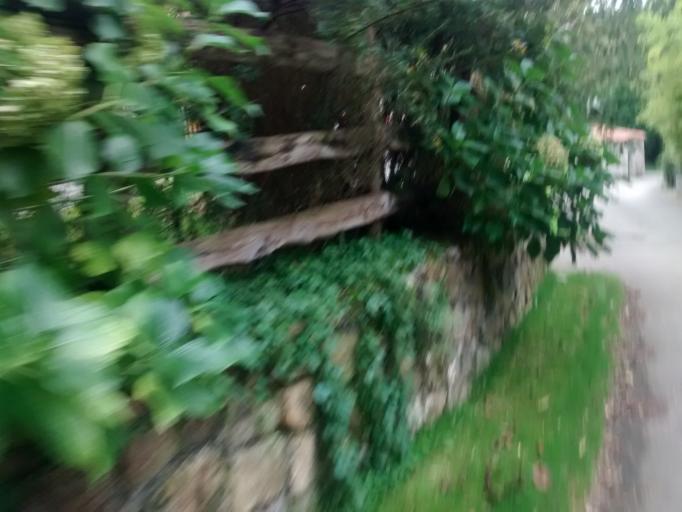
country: ES
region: Cantabria
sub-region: Provincia de Cantabria
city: Entrambasaguas
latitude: 43.3408
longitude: -3.6910
